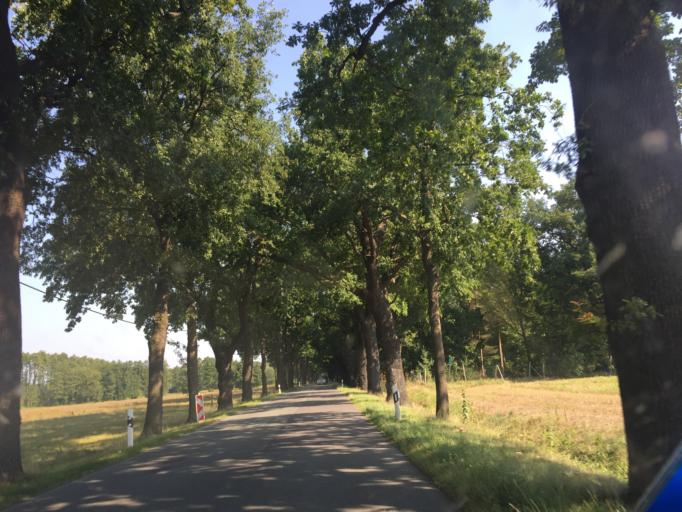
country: DE
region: Saxony
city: Uhyst
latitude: 51.3417
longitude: 14.5037
